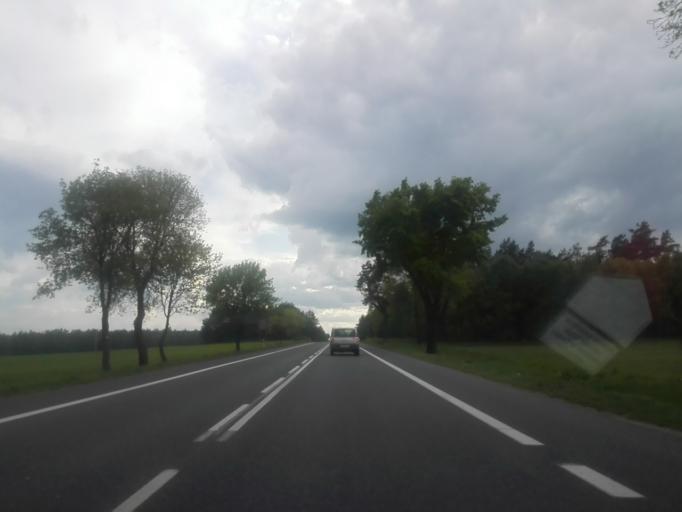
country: PL
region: Podlasie
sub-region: Powiat zambrowski
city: Szumowo
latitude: 52.8636
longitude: 22.0074
